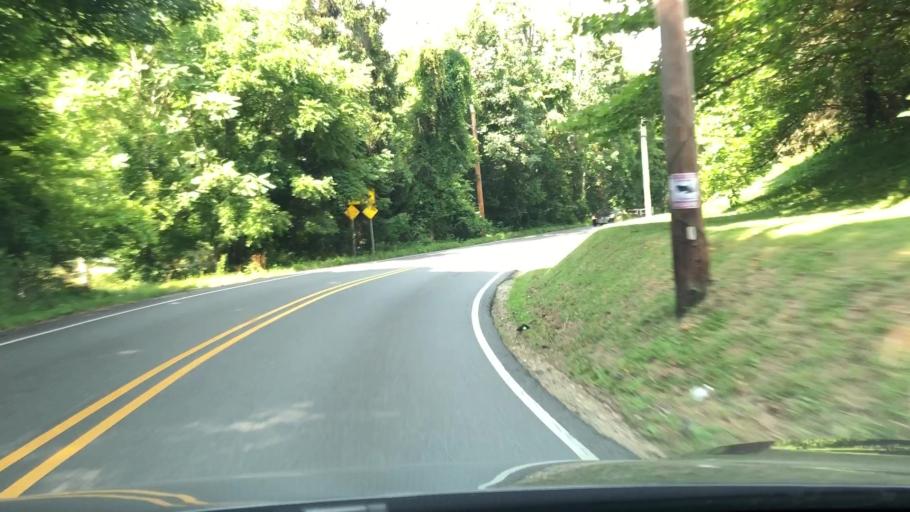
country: US
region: Pennsylvania
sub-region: Chester County
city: Berwyn
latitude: 40.0207
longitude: -75.4248
